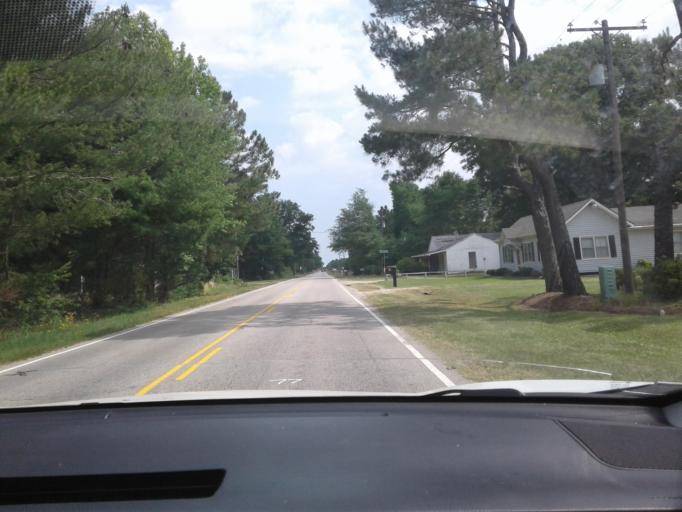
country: US
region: North Carolina
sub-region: Harnett County
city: Erwin
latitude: 35.3573
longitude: -78.6653
